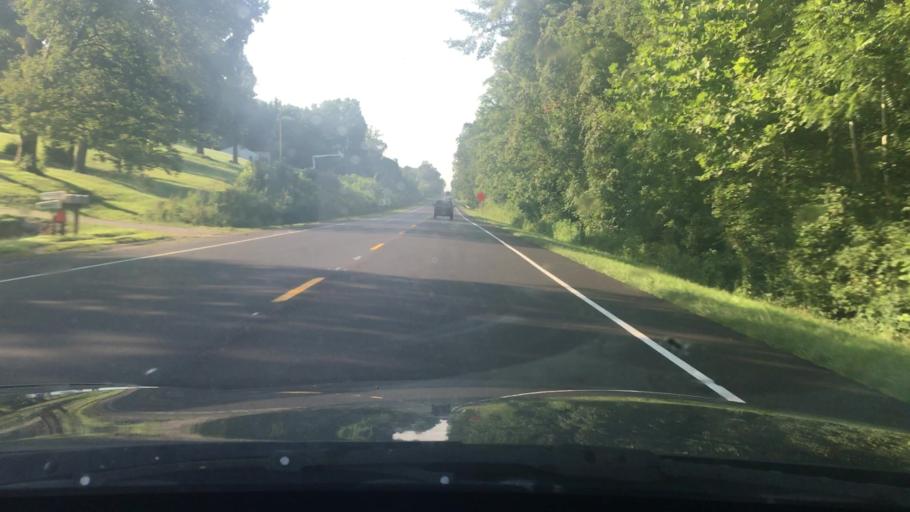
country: US
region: North Carolina
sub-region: Caswell County
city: Yanceyville
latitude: 36.4626
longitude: -79.3729
